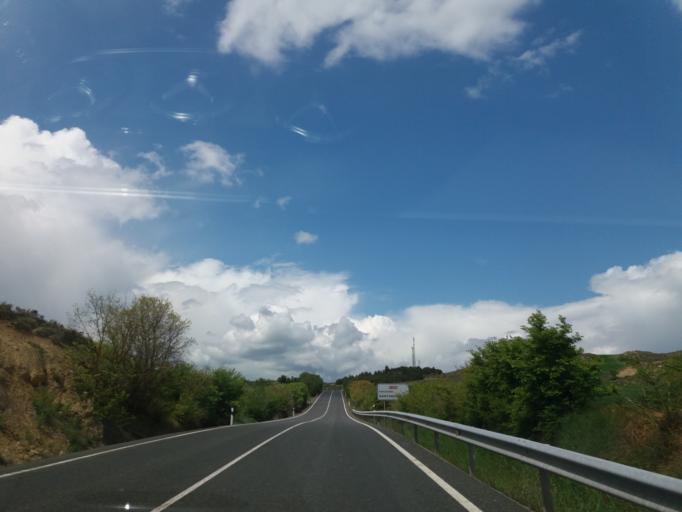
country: ES
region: La Rioja
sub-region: Provincia de La Rioja
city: Fonzaleche
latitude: 42.5690
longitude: -3.0022
